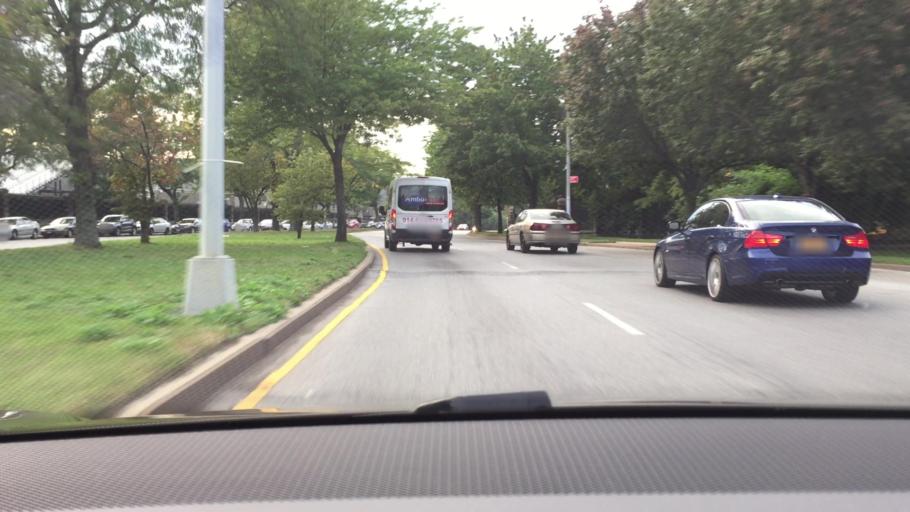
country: US
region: New York
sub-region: Bronx
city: The Bronx
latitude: 40.8617
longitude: -73.8813
